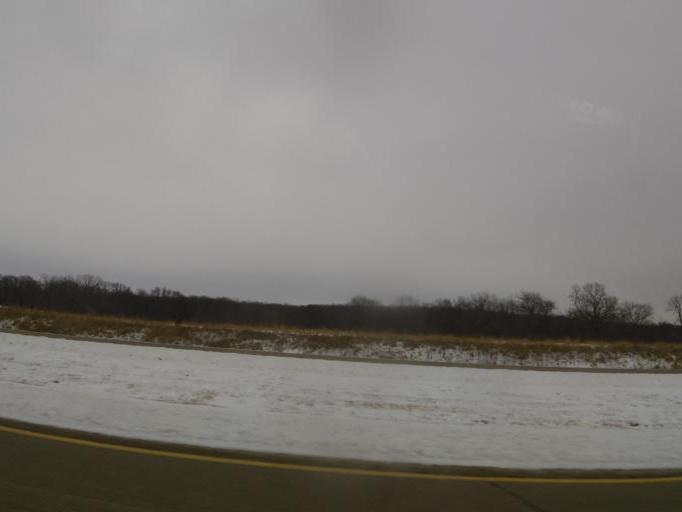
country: US
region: Illinois
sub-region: Hancock County
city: Nauvoo
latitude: 40.5747
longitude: -91.5654
